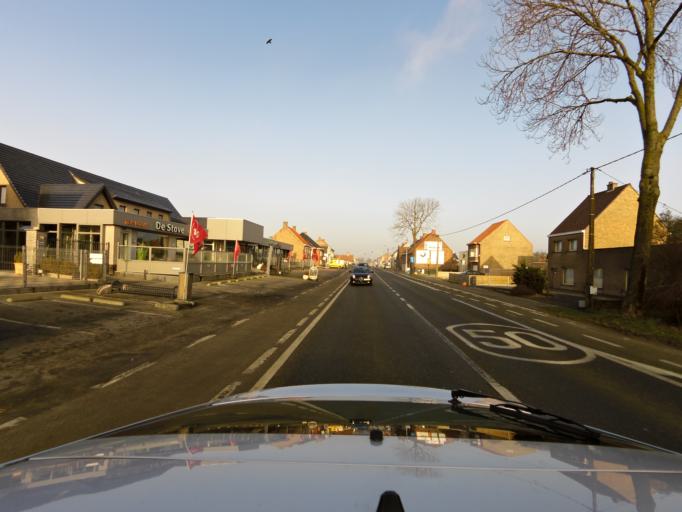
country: BE
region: Flanders
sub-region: Provincie West-Vlaanderen
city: Ichtegem
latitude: 51.1004
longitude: 3.0336
